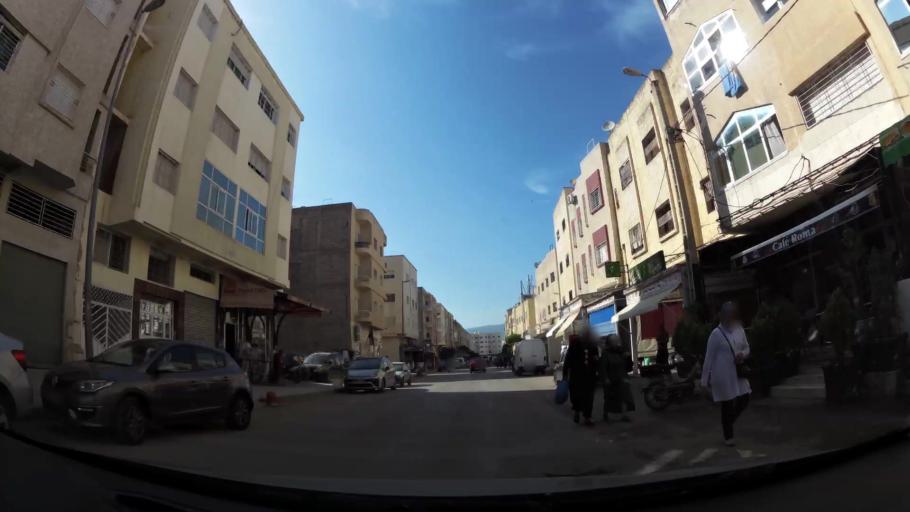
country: MA
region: Fes-Boulemane
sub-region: Fes
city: Fes
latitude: 34.0213
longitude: -5.0355
